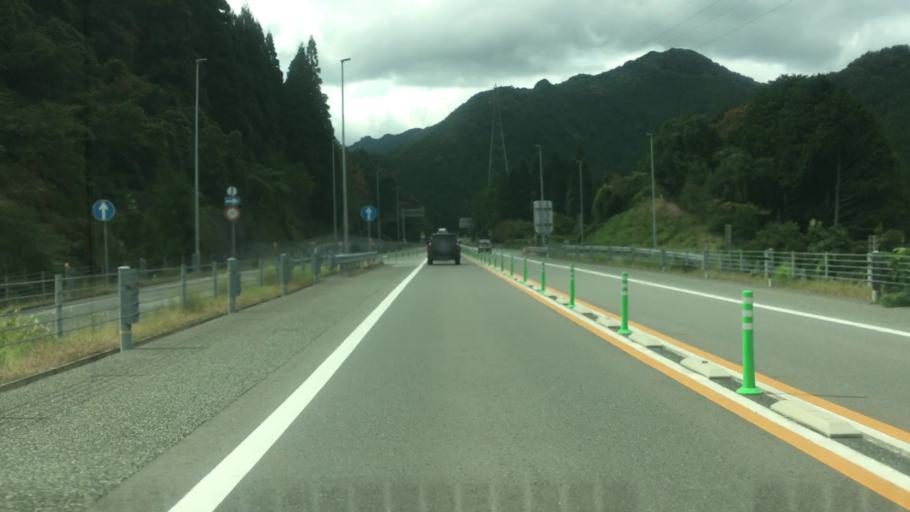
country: JP
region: Kyoto
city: Fukuchiyama
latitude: 35.2915
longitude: 134.9667
